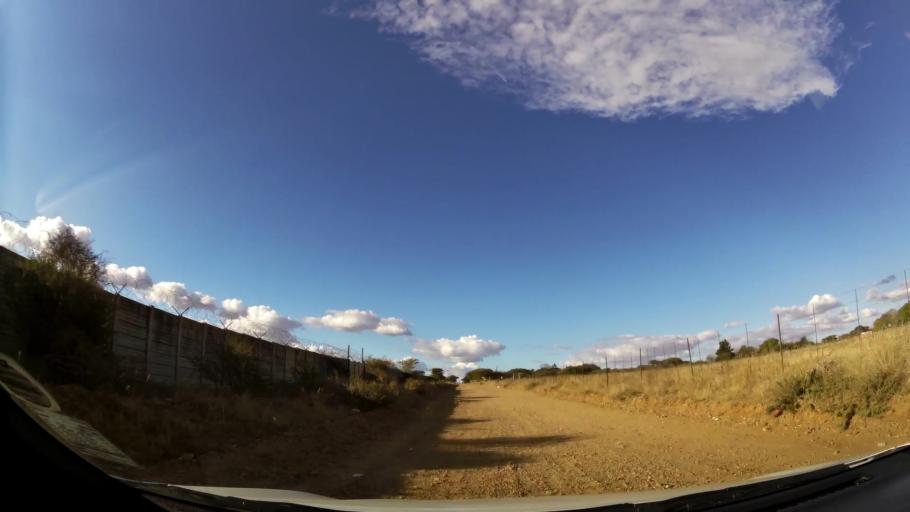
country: ZA
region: Limpopo
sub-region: Capricorn District Municipality
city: Polokwane
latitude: -23.9313
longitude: 29.4321
